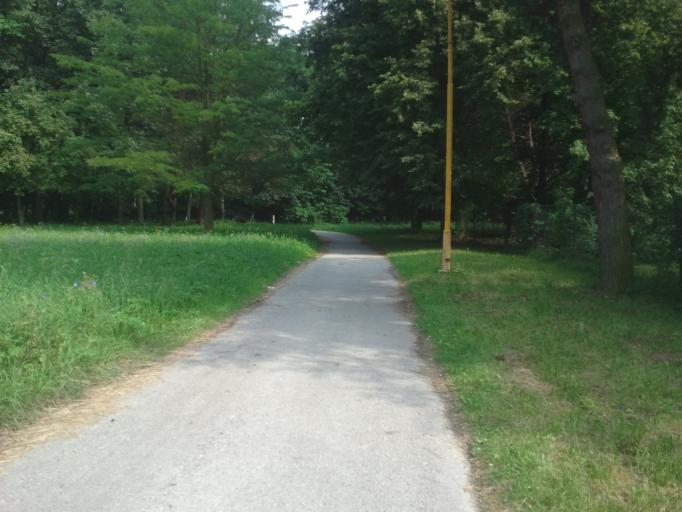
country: SK
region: Nitriansky
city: Bojnice
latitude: 48.7758
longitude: 18.5932
